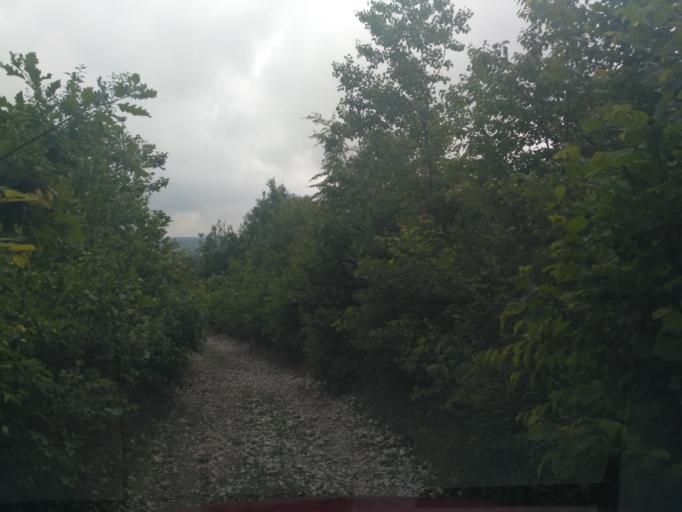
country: SK
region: Kosicky
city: Moldava nad Bodvou
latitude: 48.6930
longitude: 21.0755
